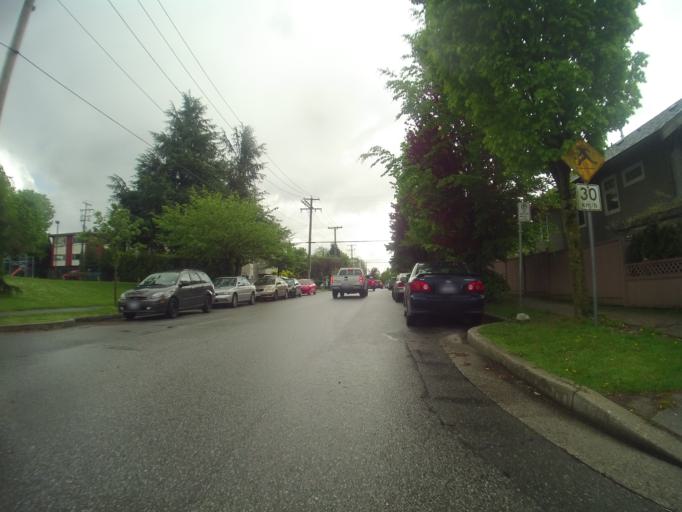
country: CA
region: British Columbia
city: Vancouver
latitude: 49.2633
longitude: -123.0737
